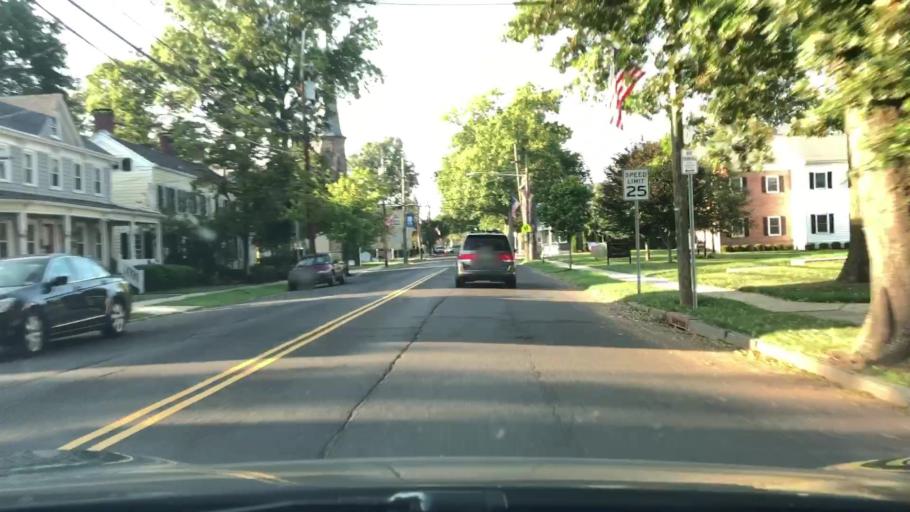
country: US
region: New Jersey
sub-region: Mercer County
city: Pennington
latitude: 40.3253
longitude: -74.7907
